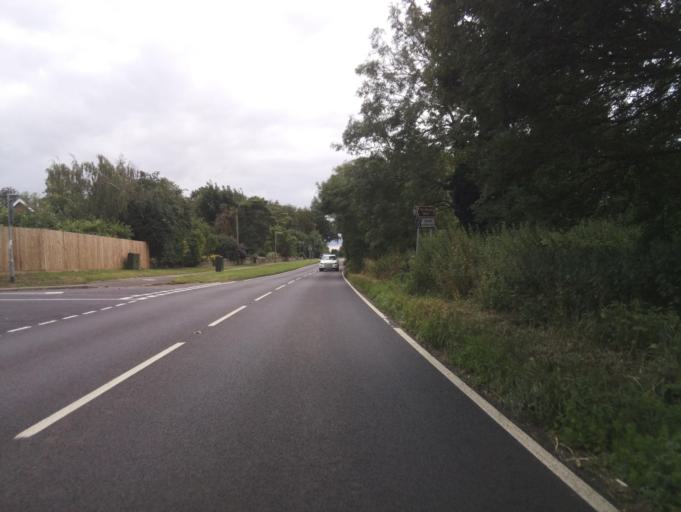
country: GB
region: England
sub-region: District of Rutland
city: Ryhall
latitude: 52.6851
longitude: -0.4739
